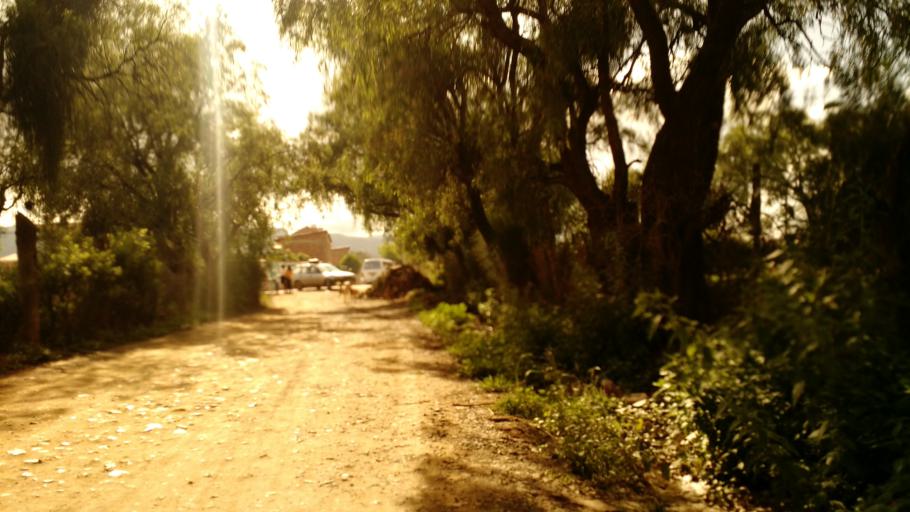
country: BO
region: Cochabamba
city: Cochabamba
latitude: -17.4557
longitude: -66.1434
